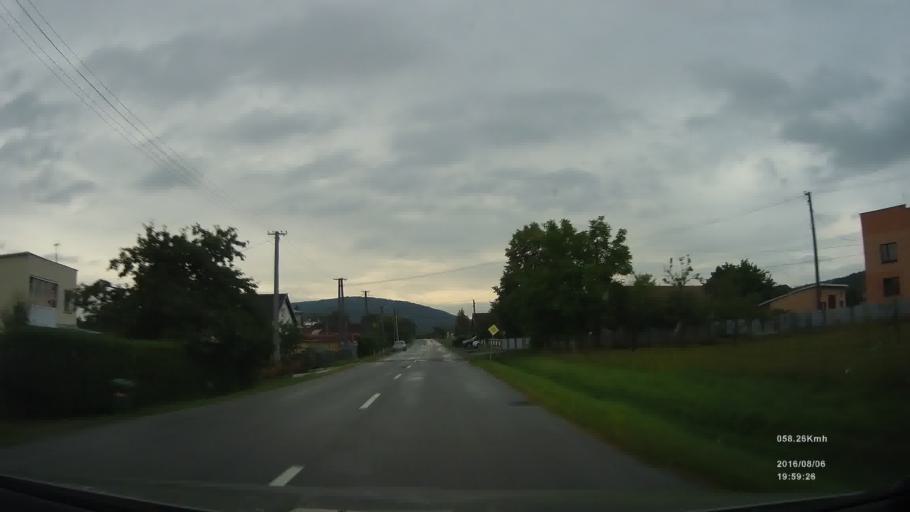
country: SK
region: Presovsky
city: Svidnik
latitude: 49.2622
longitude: 21.5802
